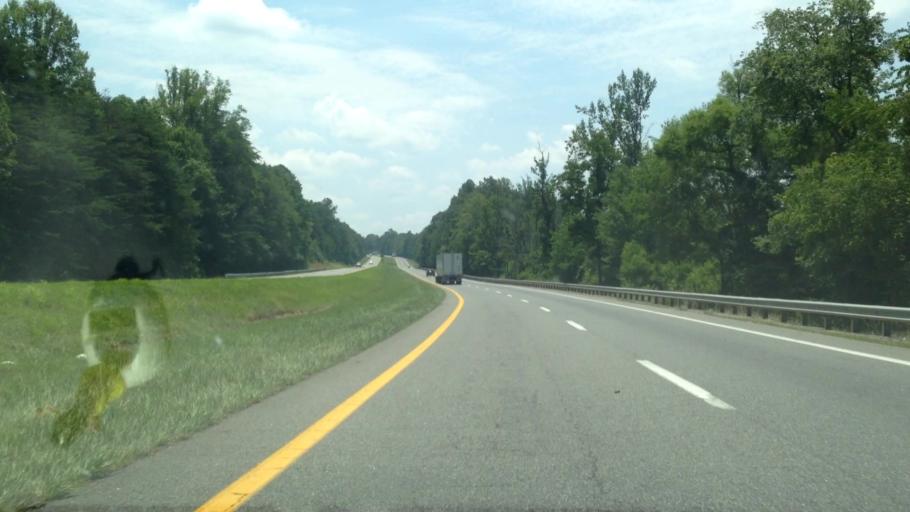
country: US
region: Virginia
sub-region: Henry County
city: Horse Pasture
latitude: 36.6596
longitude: -79.9260
